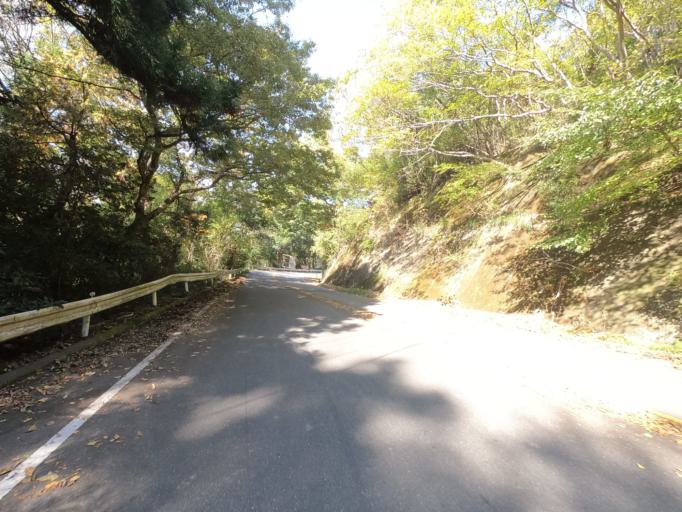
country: JP
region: Ibaraki
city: Tsukuba
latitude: 36.1672
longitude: 140.1755
